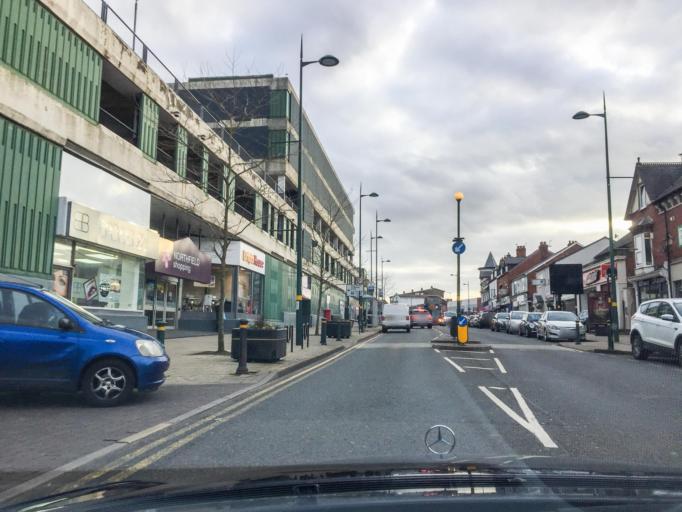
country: GB
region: England
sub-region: City and Borough of Birmingham
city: Bartley Green
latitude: 52.4174
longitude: -1.9683
